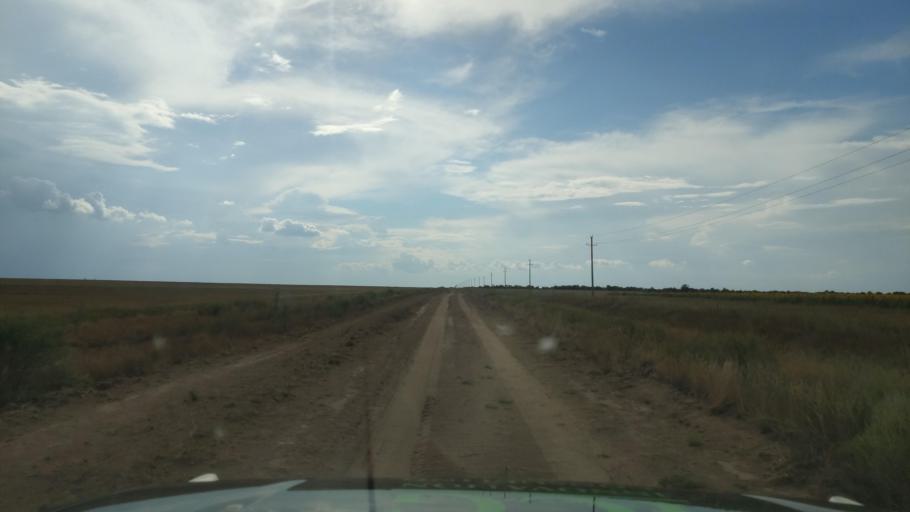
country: KZ
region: Pavlodar
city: Pavlodar
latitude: 52.5123
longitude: 77.5254
